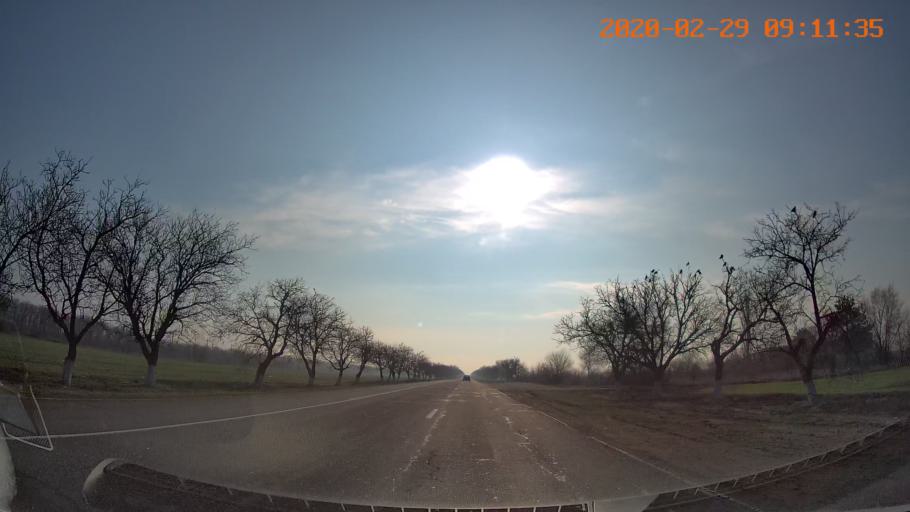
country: MD
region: Telenesti
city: Slobozia
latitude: 46.8339
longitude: 29.8024
